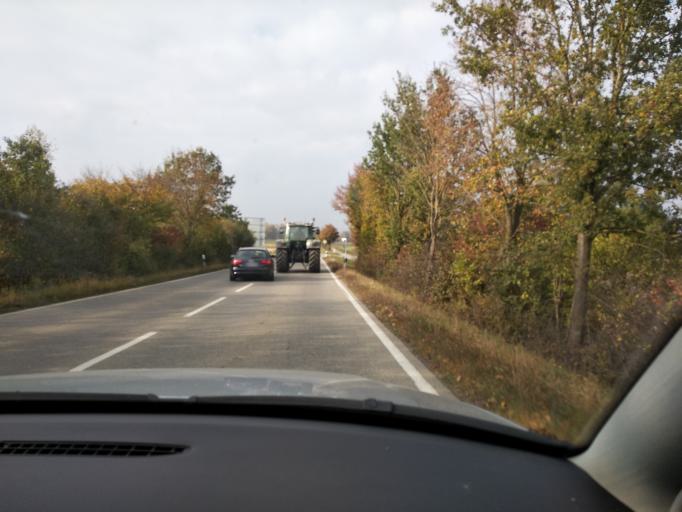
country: DE
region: Bavaria
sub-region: Upper Bavaria
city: Forstinning
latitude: 48.1724
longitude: 11.8884
